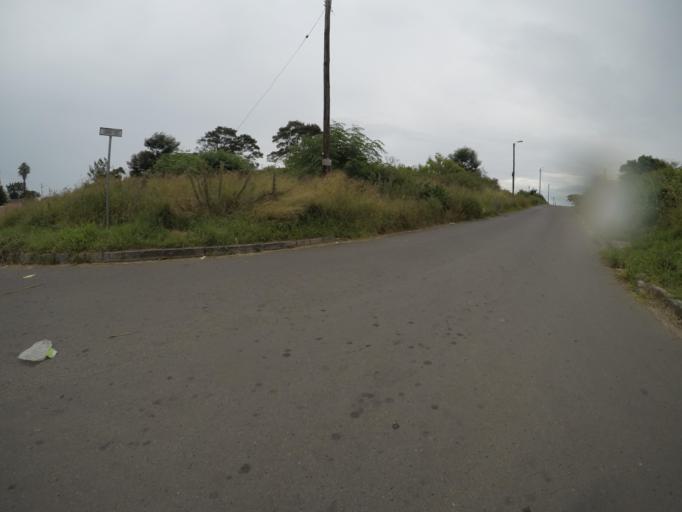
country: ZA
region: Eastern Cape
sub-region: Buffalo City Metropolitan Municipality
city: East London
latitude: -32.9976
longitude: 27.8488
